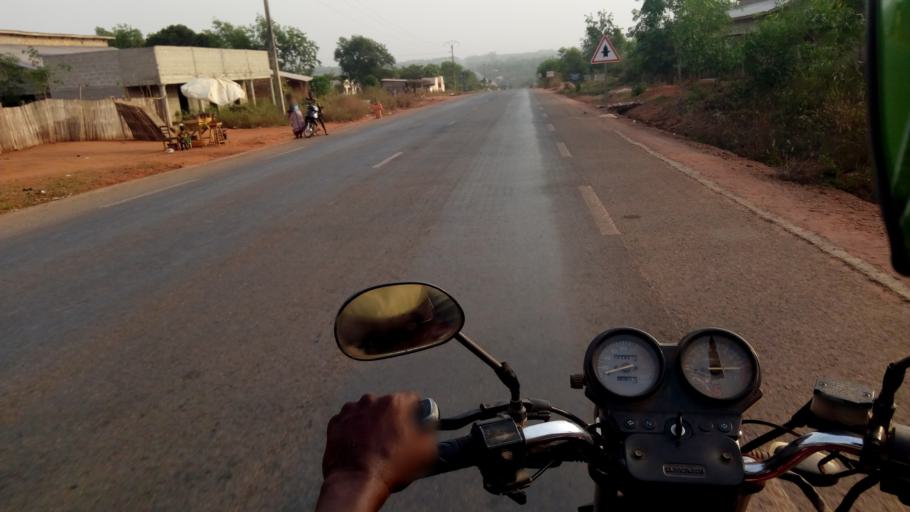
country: BJ
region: Atlantique
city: Hinvi
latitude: 6.6988
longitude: 2.2892
